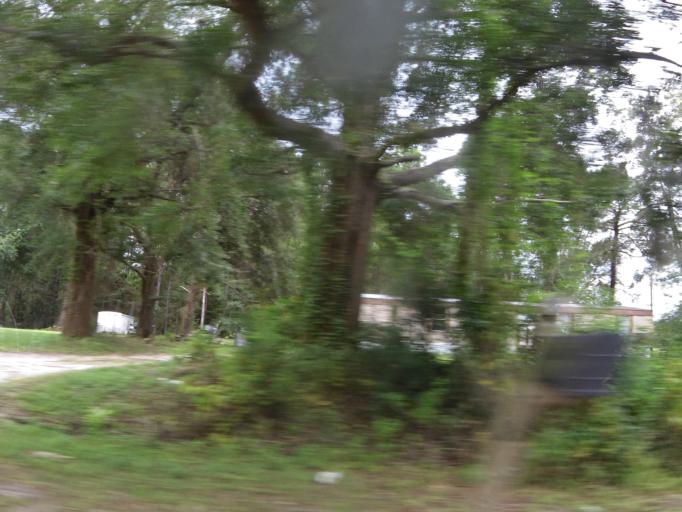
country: US
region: Florida
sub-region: Clay County
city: Middleburg
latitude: 30.1171
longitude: -81.9491
